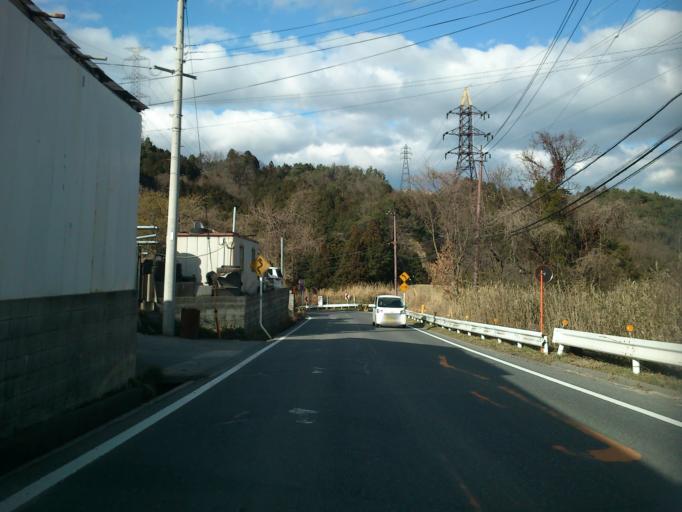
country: JP
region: Shiga Prefecture
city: Otsu-shi
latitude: 35.0376
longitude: 135.8459
